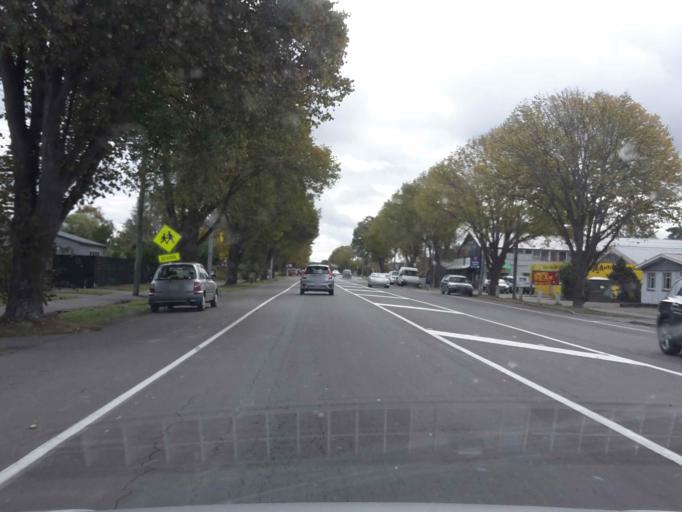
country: NZ
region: Canterbury
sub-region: Christchurch City
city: Christchurch
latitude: -43.4903
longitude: 172.6208
